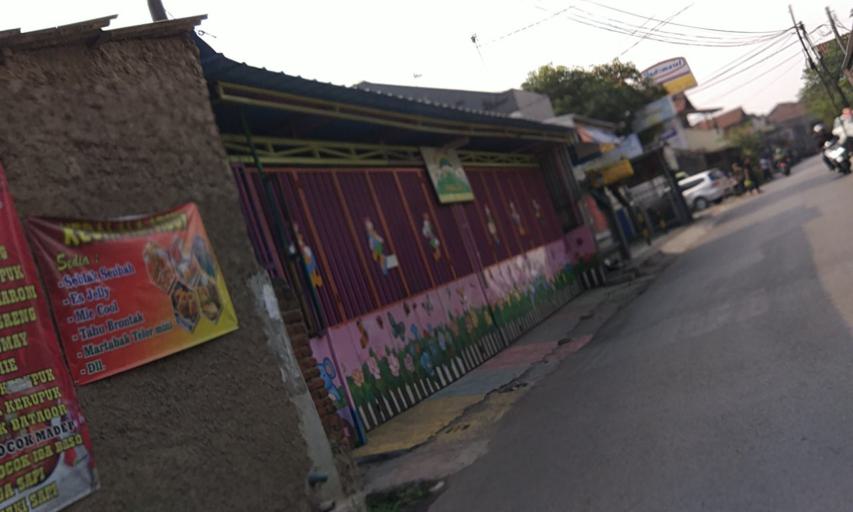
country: ID
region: West Java
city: Margahayukencana
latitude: -6.9722
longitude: 107.5565
